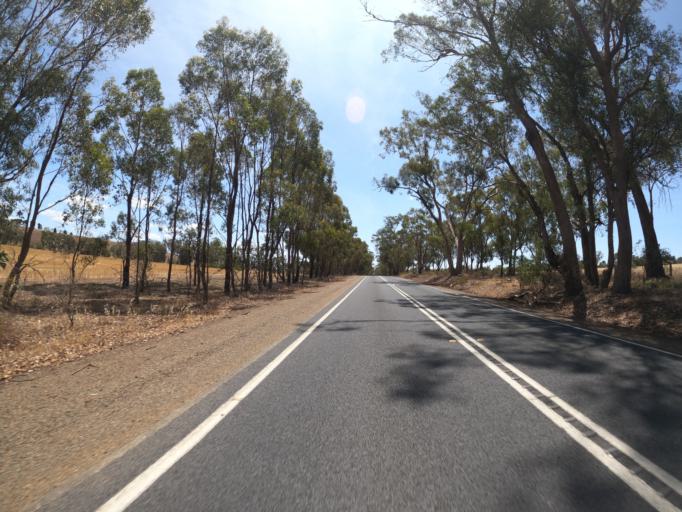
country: AU
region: Victoria
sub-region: Benalla
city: Benalla
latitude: -36.3736
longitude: 145.9737
